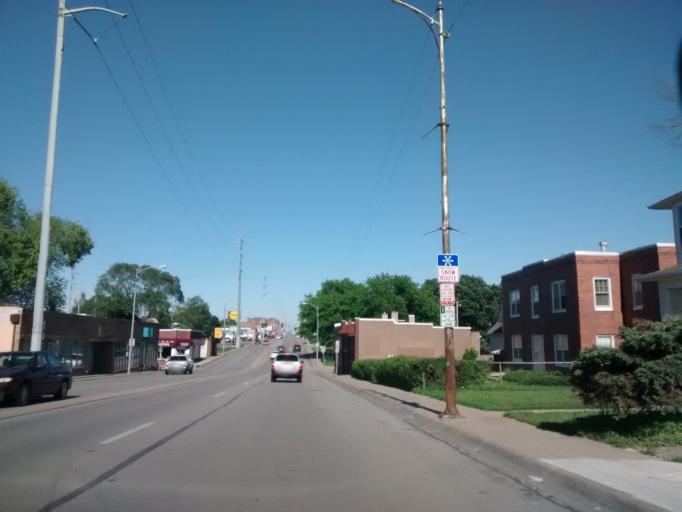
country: US
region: Nebraska
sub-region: Douglas County
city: Omaha
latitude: 41.2523
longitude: -95.9648
